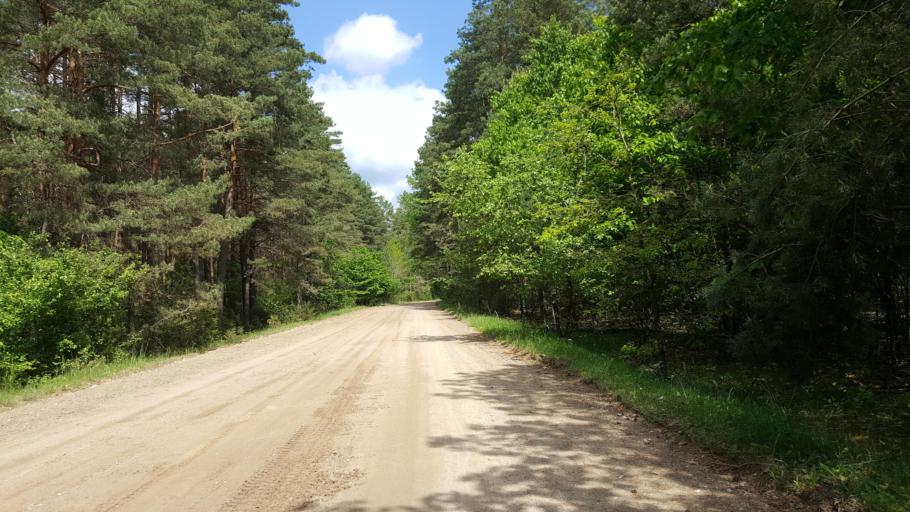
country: BY
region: Brest
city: Kamyanyets
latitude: 52.4707
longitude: 23.9681
